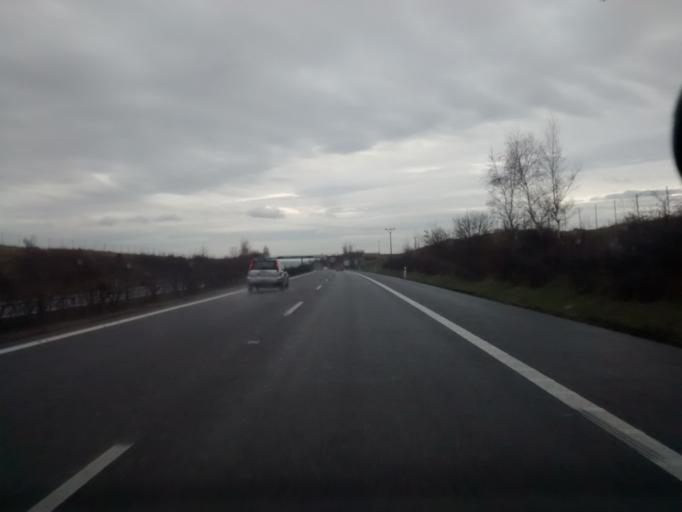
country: CZ
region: Central Bohemia
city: Nelahozeves
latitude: 50.3316
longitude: 14.2892
